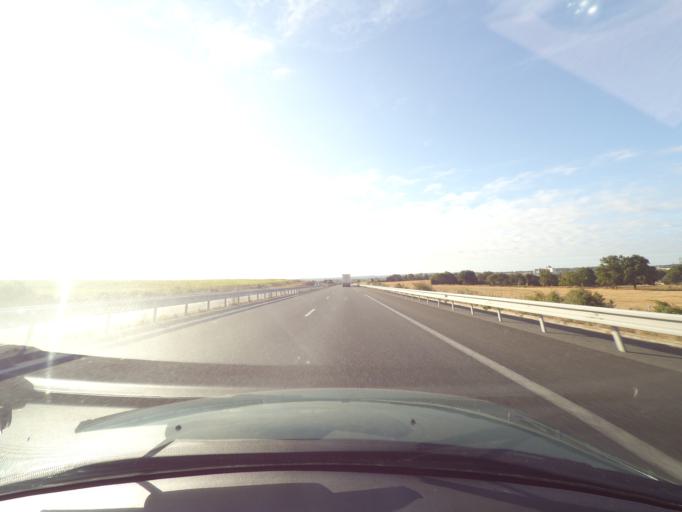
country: FR
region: Poitou-Charentes
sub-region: Departement des Deux-Sevres
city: Combrand
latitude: 46.9187
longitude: -0.6939
